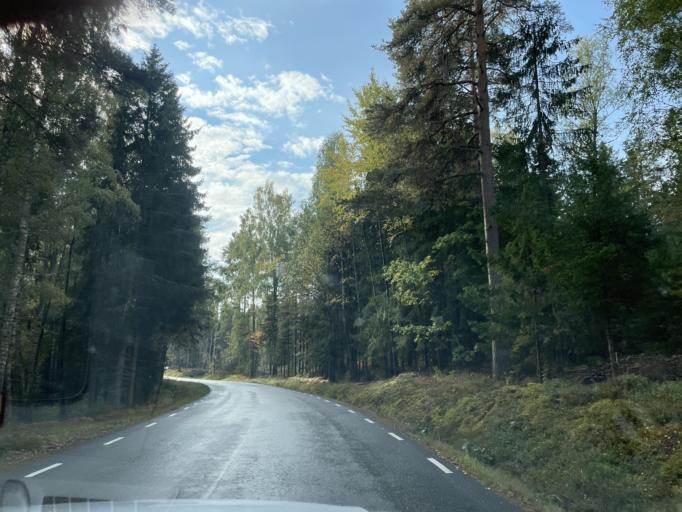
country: SE
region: Vaermland
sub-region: Karlstads Kommun
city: Skattkarr
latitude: 59.4059
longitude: 13.6027
